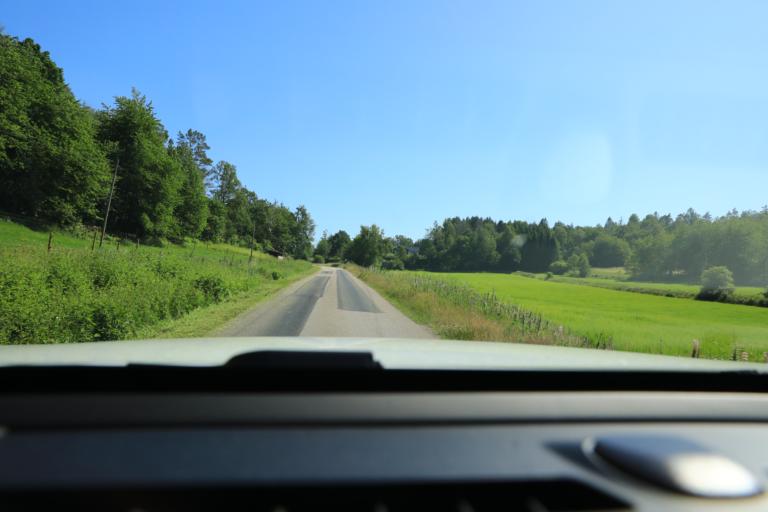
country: SE
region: Halland
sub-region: Varbergs Kommun
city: Veddige
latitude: 57.1954
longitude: 12.3224
